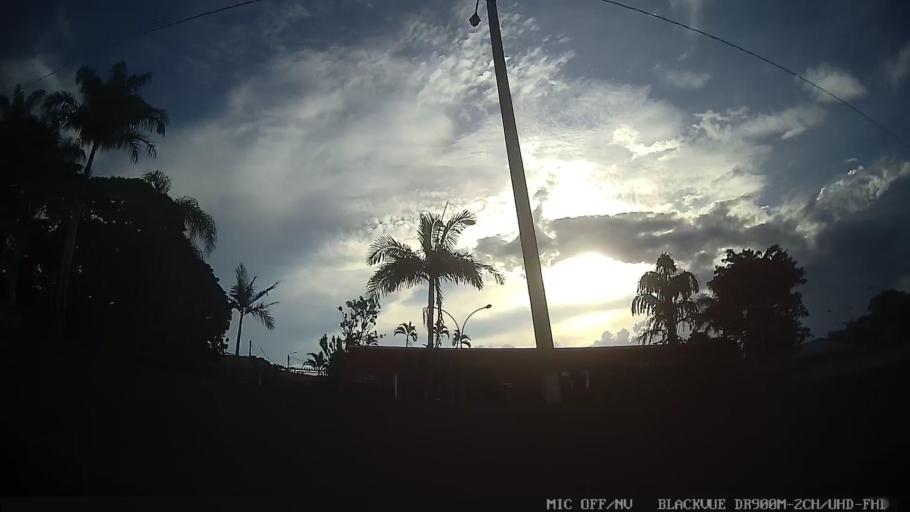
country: BR
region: Sao Paulo
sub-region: Tiete
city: Tiete
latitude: -23.0807
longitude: -47.7221
